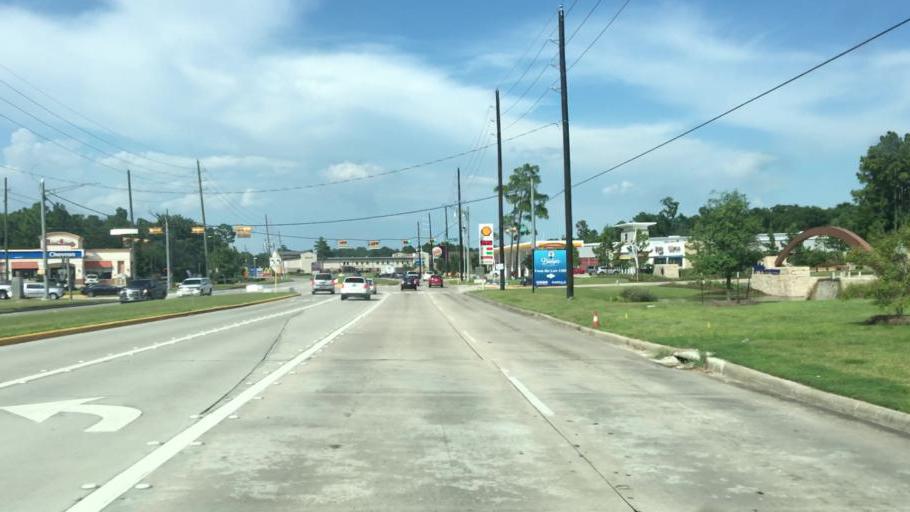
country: US
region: Texas
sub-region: Harris County
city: Atascocita
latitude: 29.9797
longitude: -95.1656
